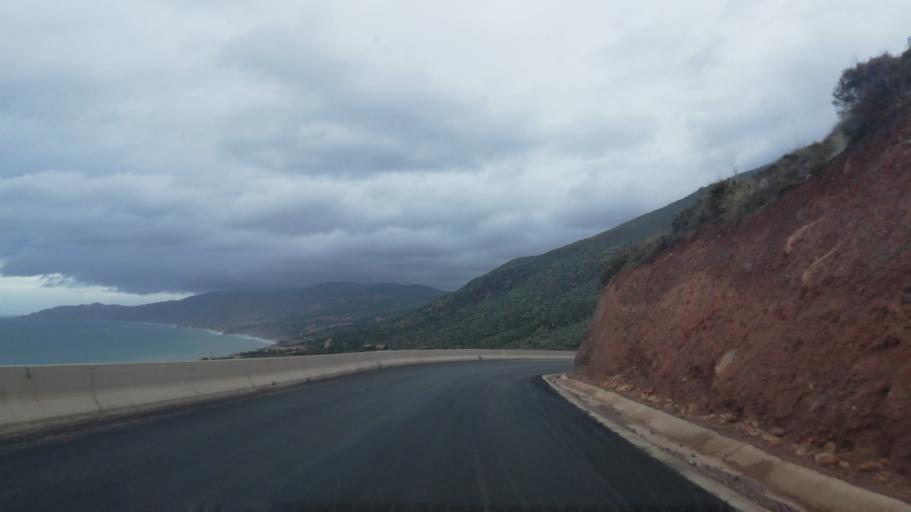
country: DZ
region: Oran
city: Bir el Djir
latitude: 35.7692
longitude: -0.5199
